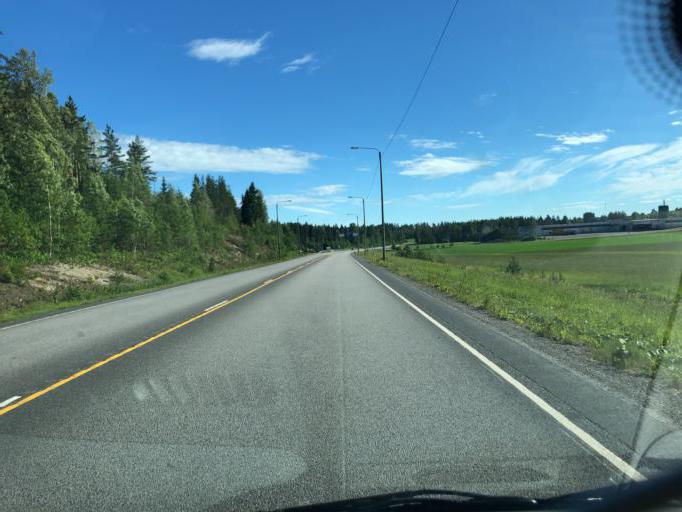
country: FI
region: Uusimaa
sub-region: Loviisa
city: Liljendal
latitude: 60.5752
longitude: 26.0721
